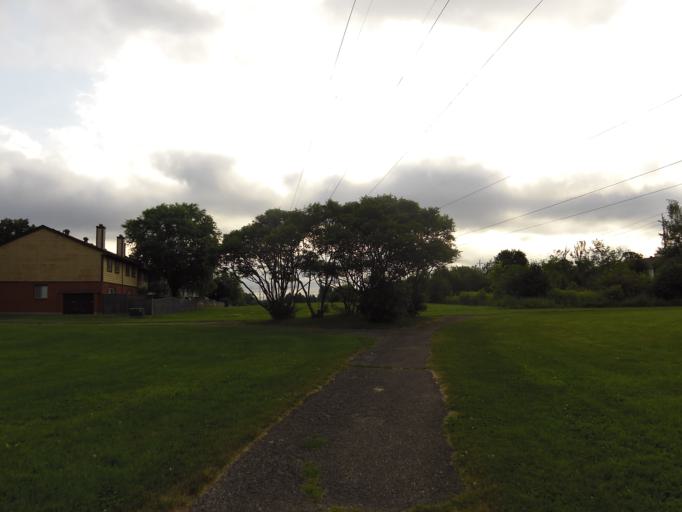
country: CA
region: Ontario
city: Ottawa
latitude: 45.3357
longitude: -75.7438
